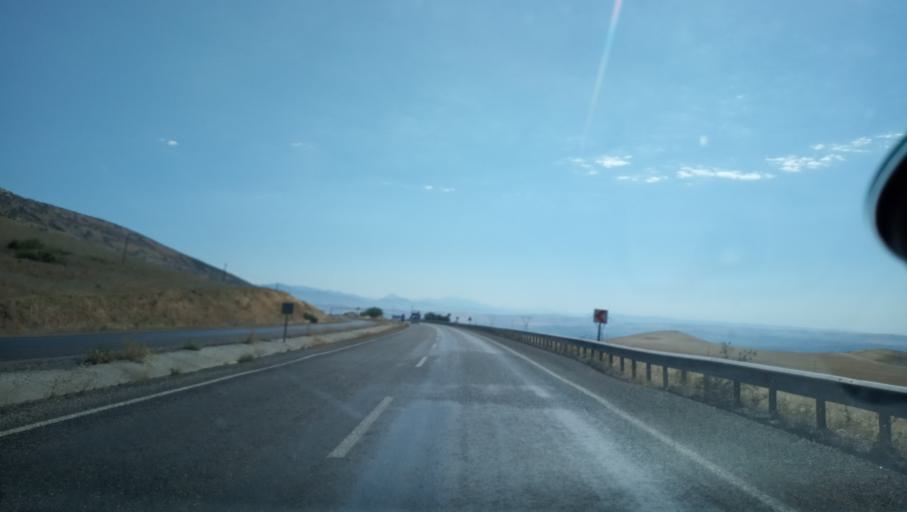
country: TR
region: Diyarbakir
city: Malabadi
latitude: 38.1184
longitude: 41.1433
